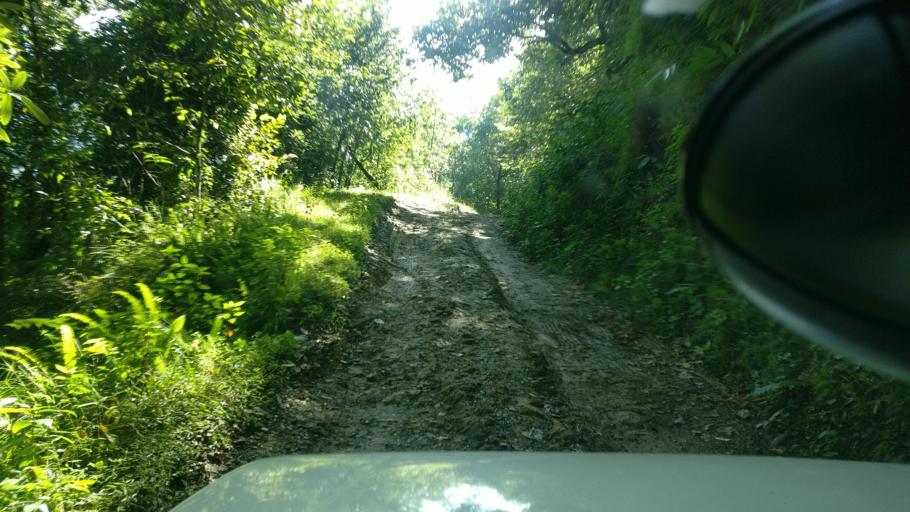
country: NP
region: Western Region
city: Baglung
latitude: 28.1315
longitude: 83.6612
